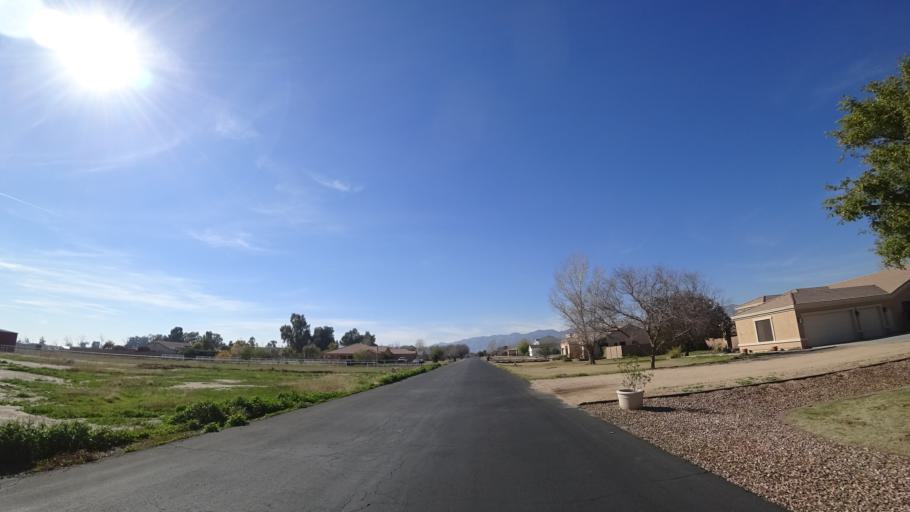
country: US
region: Arizona
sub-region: Maricopa County
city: Citrus Park
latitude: 33.5054
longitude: -112.4645
